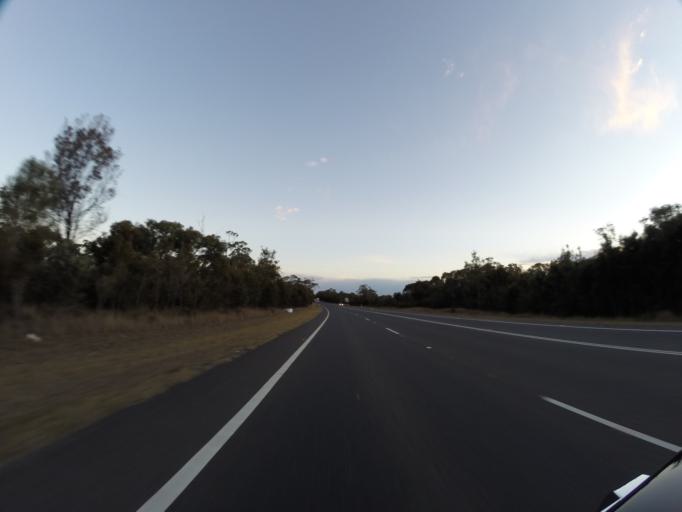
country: AU
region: New South Wales
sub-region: Liverpool
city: Holsworthy
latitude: -34.0334
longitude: 150.9614
